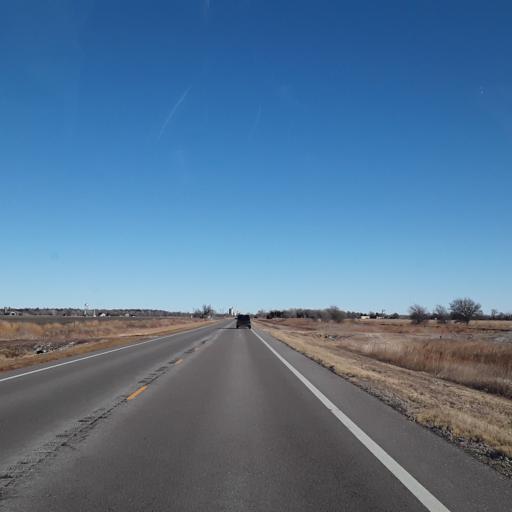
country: US
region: Kansas
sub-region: Pawnee County
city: Larned
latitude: 38.1520
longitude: -99.1330
